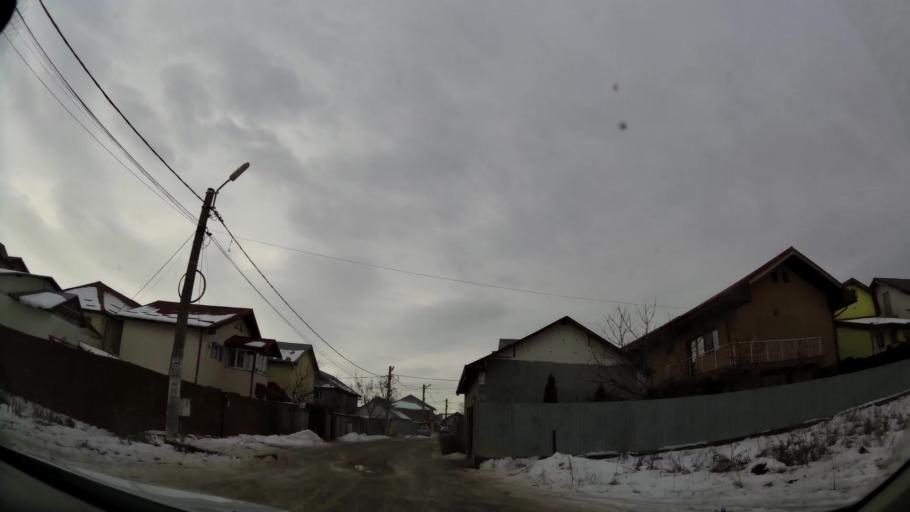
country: RO
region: Ilfov
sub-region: Comuna Pantelimon
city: Pantelimon
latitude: 44.4581
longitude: 26.1995
